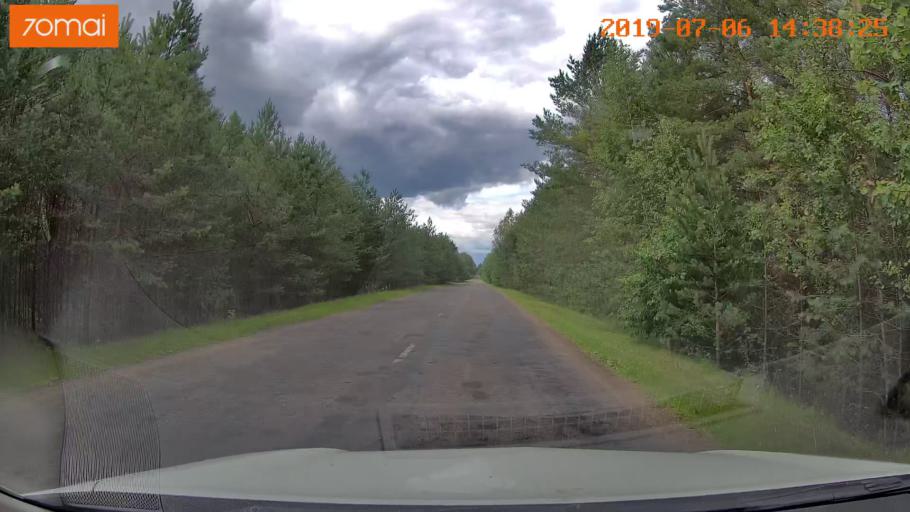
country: BY
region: Minsk
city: Ivyanyets
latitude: 53.9059
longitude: 26.7030
